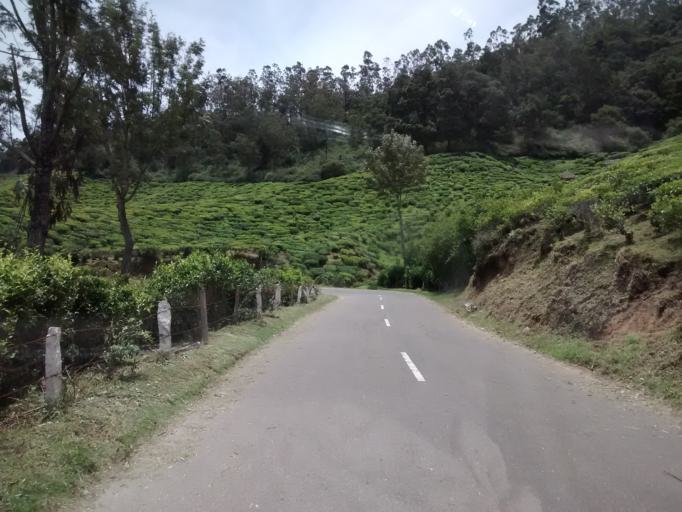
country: IN
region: Kerala
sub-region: Idukki
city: Munnar
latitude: 10.1397
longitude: 77.1960
